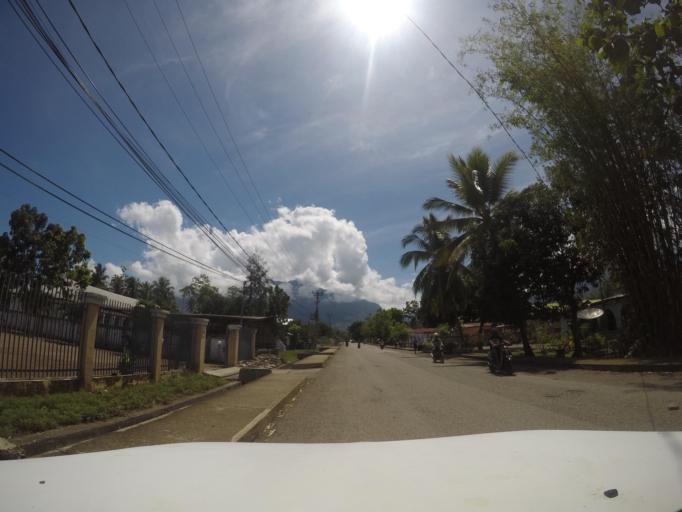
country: TL
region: Bobonaro
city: Maliana
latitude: -8.9892
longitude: 125.2110
